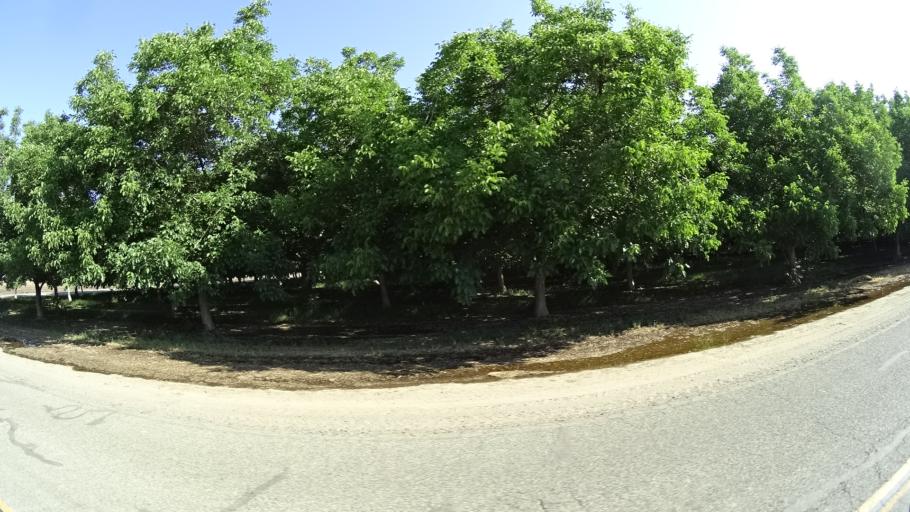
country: US
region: California
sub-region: Kings County
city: Lucerne
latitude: 36.3864
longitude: -119.6186
